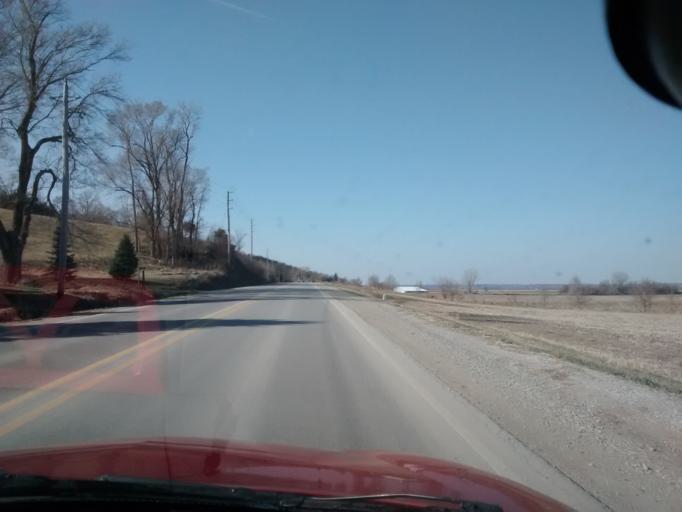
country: US
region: Iowa
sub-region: Pottawattamie County
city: Carter Lake
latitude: 41.3856
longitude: -95.8446
